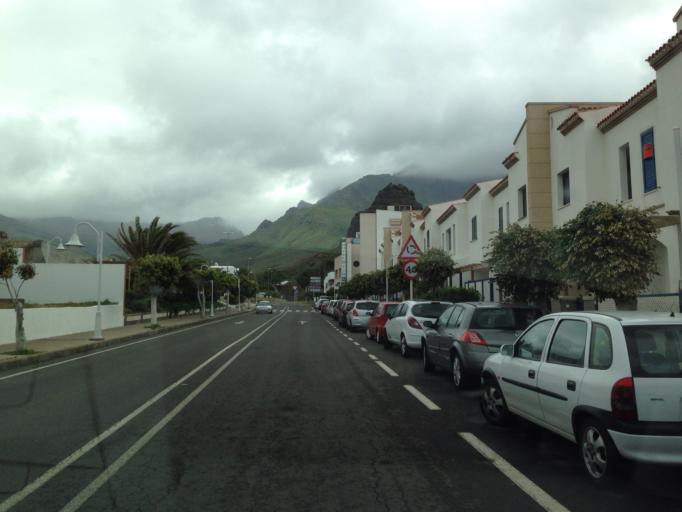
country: ES
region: Canary Islands
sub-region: Provincia de Las Palmas
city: Agaete
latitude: 28.1035
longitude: -15.7111
